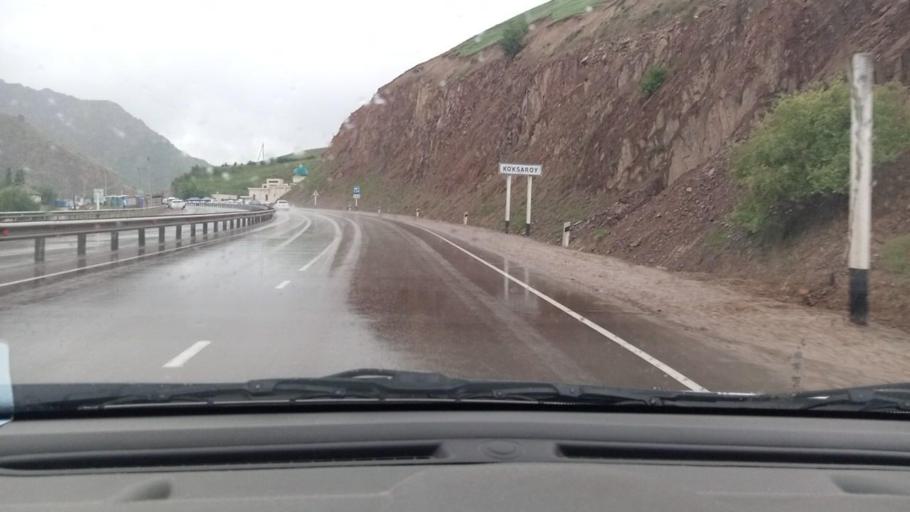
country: UZ
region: Toshkent
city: Angren
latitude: 41.1083
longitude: 70.3353
